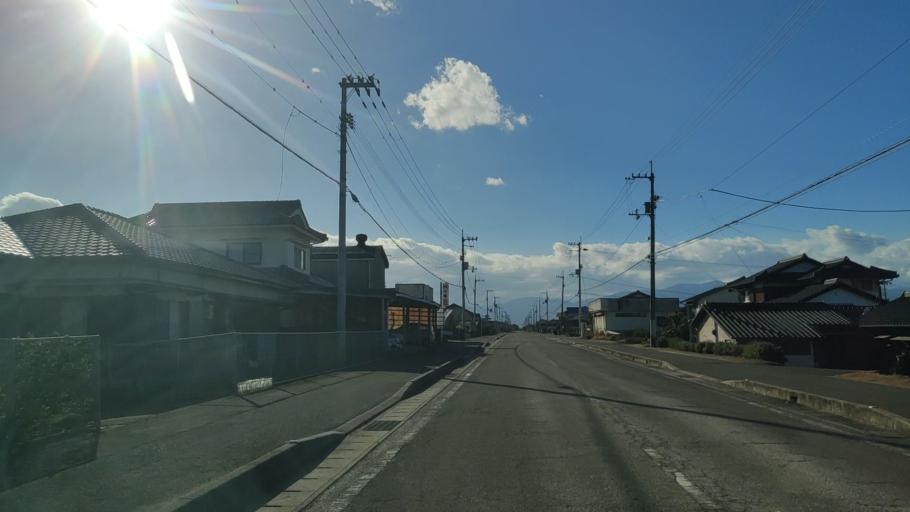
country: JP
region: Ehime
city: Saijo
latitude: 33.9304
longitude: 133.1631
